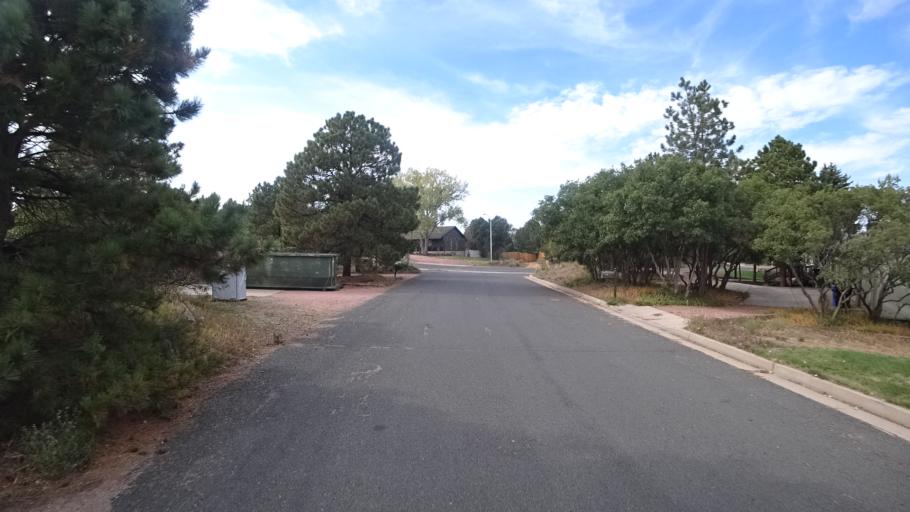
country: US
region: Colorado
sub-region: El Paso County
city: Colorado Springs
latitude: 38.8952
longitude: -104.7767
